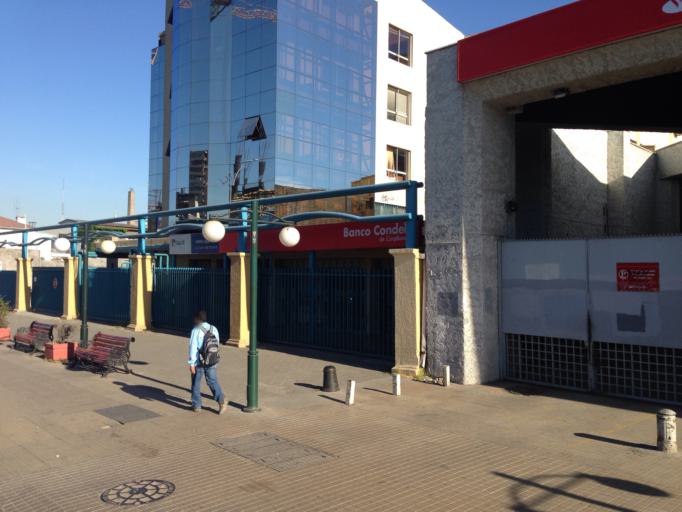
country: CL
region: Santiago Metropolitan
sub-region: Provincia de Santiago
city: Villa Presidente Frei, Nunoa, Santiago, Chile
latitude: -33.4540
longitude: -70.6054
